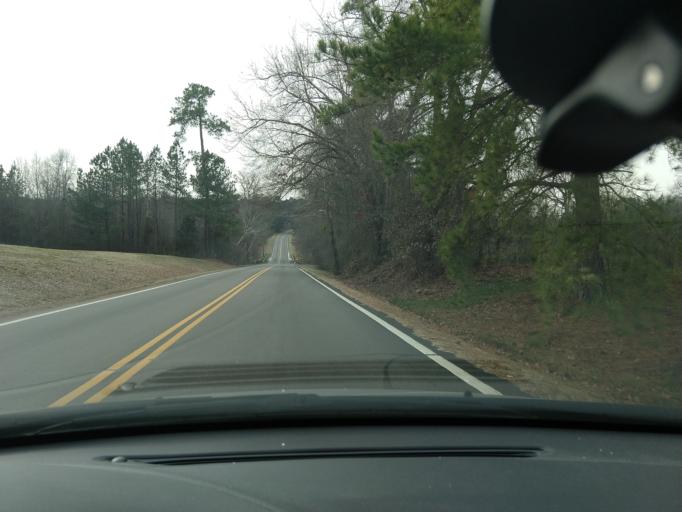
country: US
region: South Carolina
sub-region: Spartanburg County
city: Cowpens
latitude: 35.0426
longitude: -81.7985
